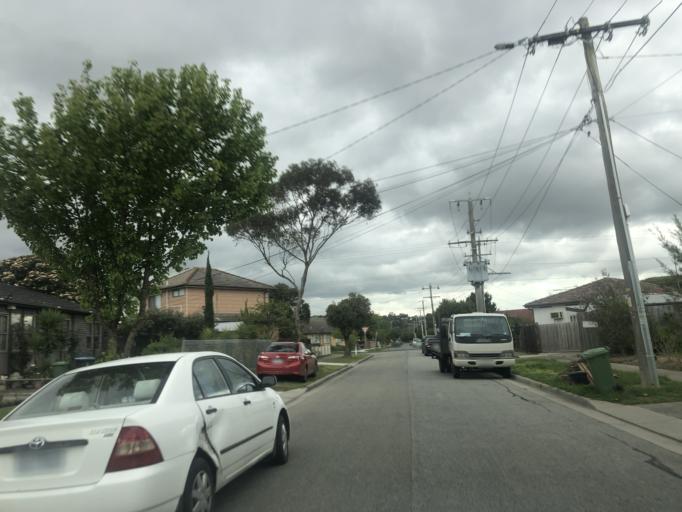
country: AU
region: Victoria
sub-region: Casey
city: Doveton
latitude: -37.9802
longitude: 145.2353
